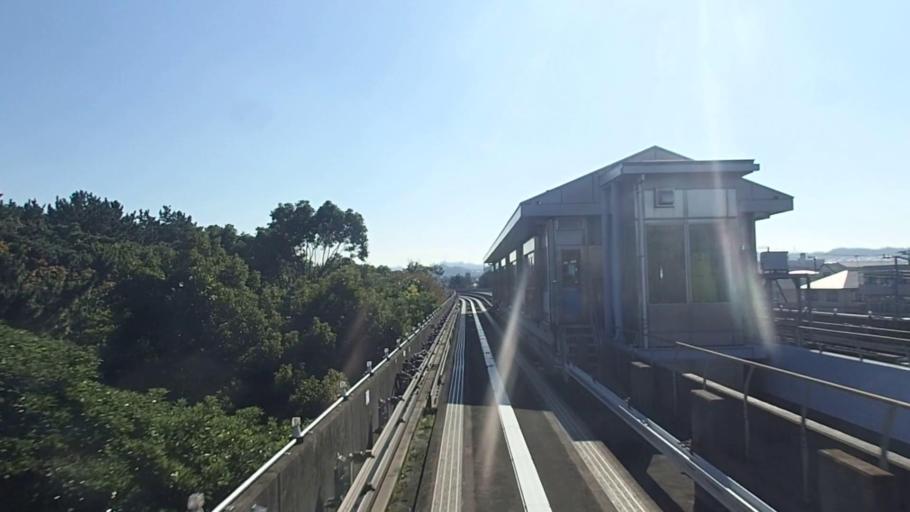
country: JP
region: Kanagawa
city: Yokosuka
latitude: 35.3376
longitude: 139.6322
